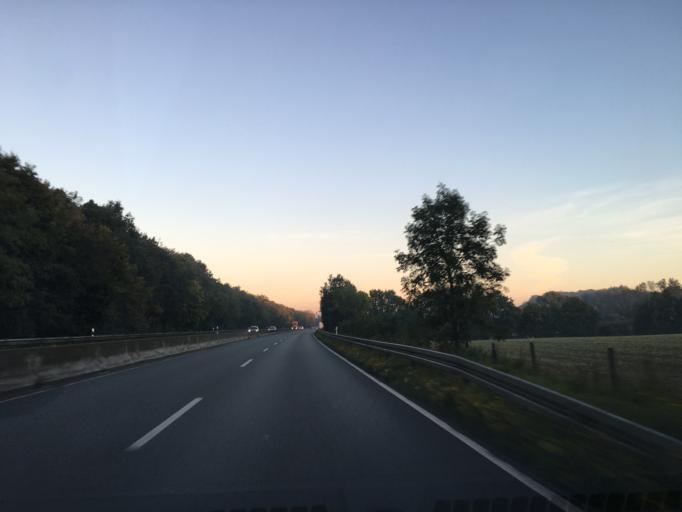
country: DE
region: North Rhine-Westphalia
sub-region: Regierungsbezirk Munster
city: Altenberge
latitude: 52.0077
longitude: 7.5077
